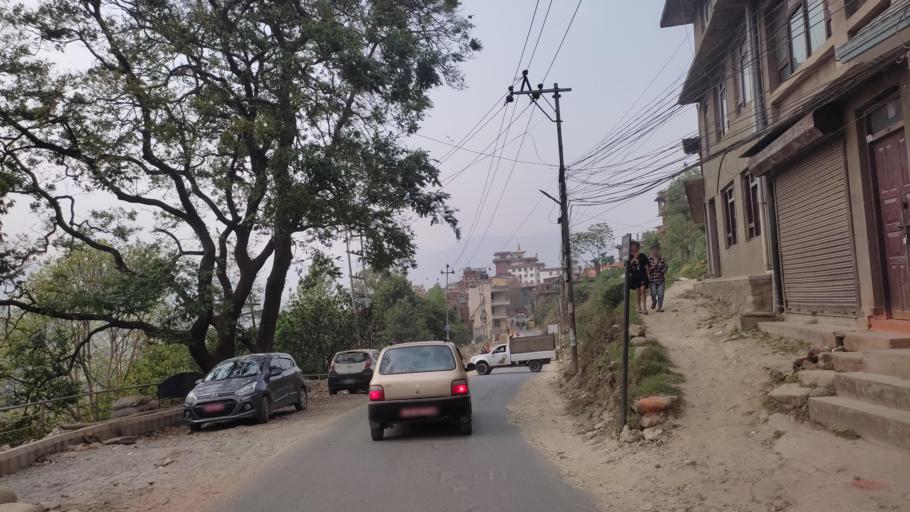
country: NP
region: Central Region
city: Kirtipur
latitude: 27.6803
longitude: 85.2727
